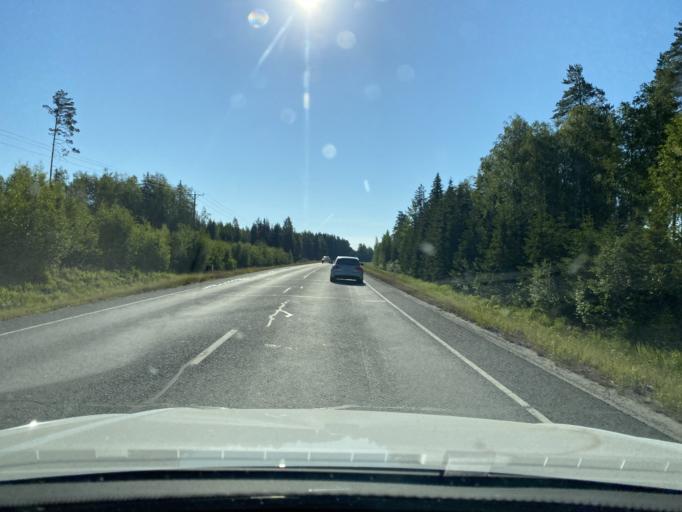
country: FI
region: Haeme
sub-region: Forssa
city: Tammela
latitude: 60.8299
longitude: 23.8702
